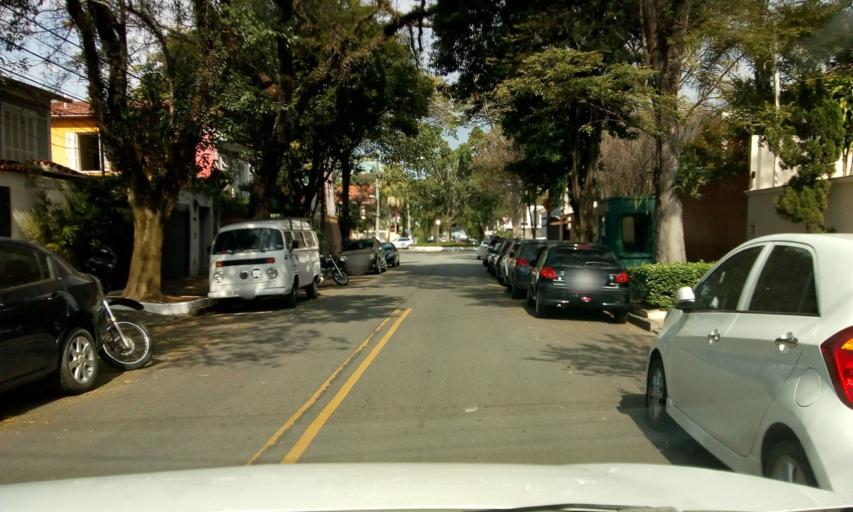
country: BR
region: Sao Paulo
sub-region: Sao Paulo
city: Sao Paulo
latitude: -23.5802
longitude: -46.6692
